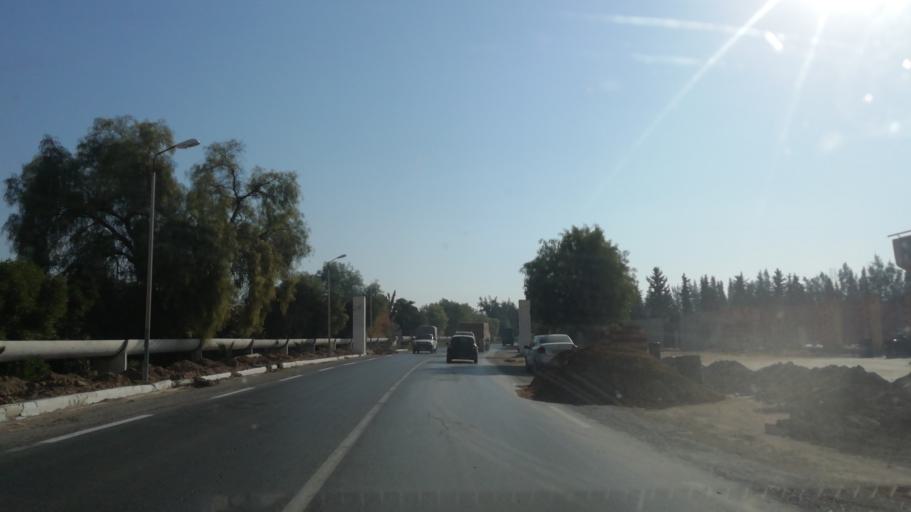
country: DZ
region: Relizane
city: Relizane
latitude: 35.7338
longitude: 0.4683
